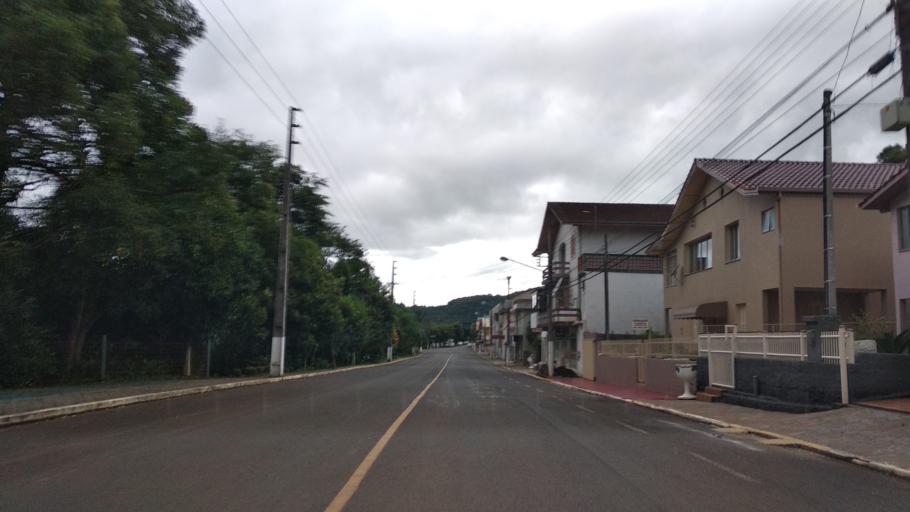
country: BR
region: Santa Catarina
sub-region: Videira
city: Videira
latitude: -27.0478
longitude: -51.2307
